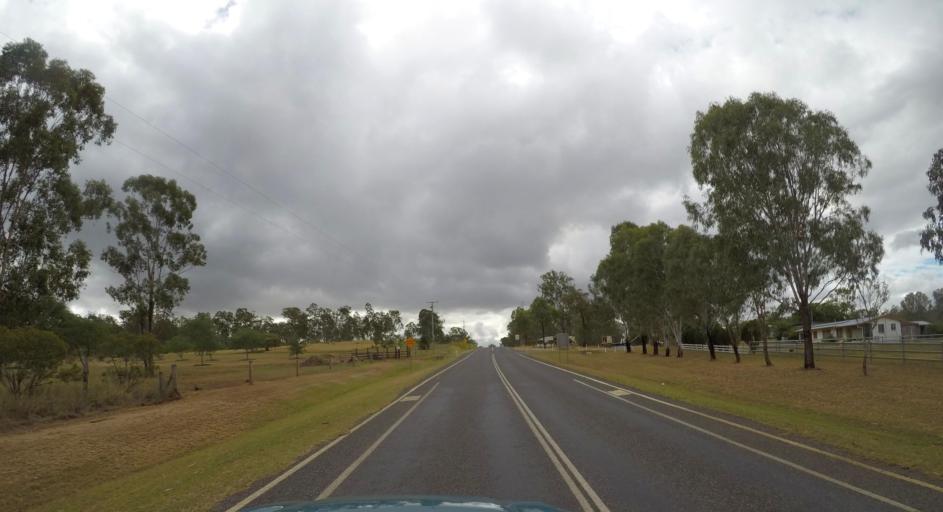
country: AU
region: Queensland
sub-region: North Burnett
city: Gayndah
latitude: -25.3631
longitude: 151.1200
